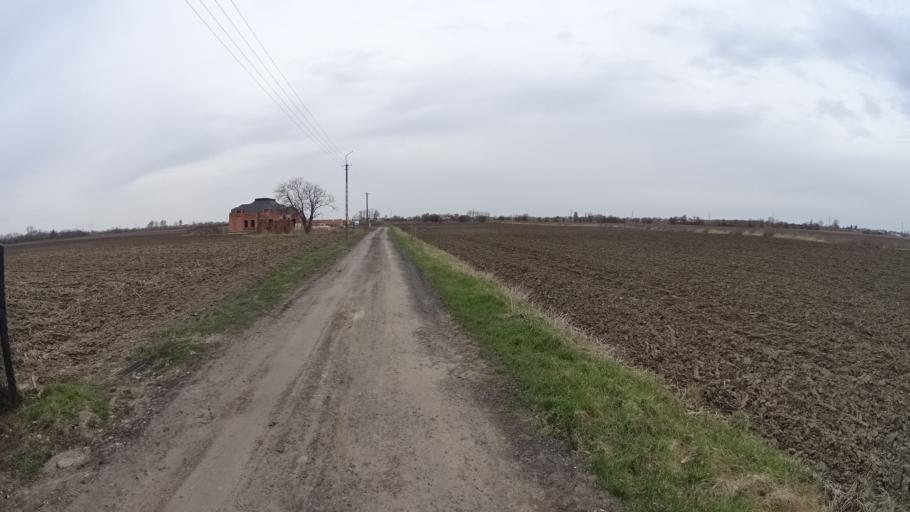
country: PL
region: Masovian Voivodeship
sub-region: Powiat warszawski zachodni
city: Stare Babice
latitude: 52.2442
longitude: 20.8077
